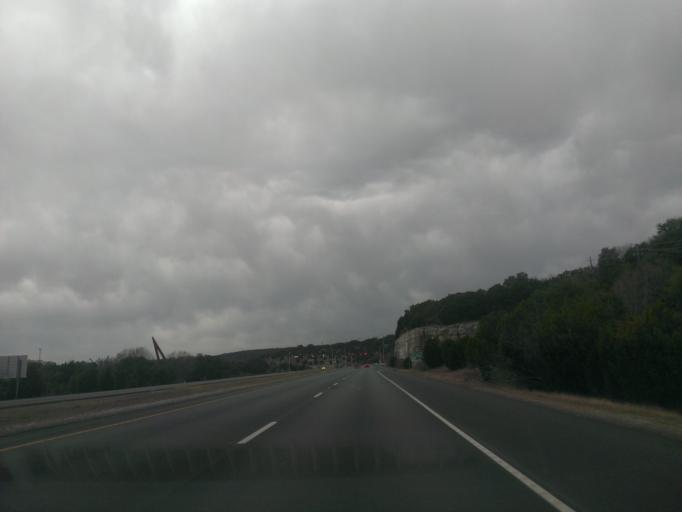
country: US
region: Texas
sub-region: Williamson County
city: Jollyville
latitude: 30.3882
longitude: -97.7567
